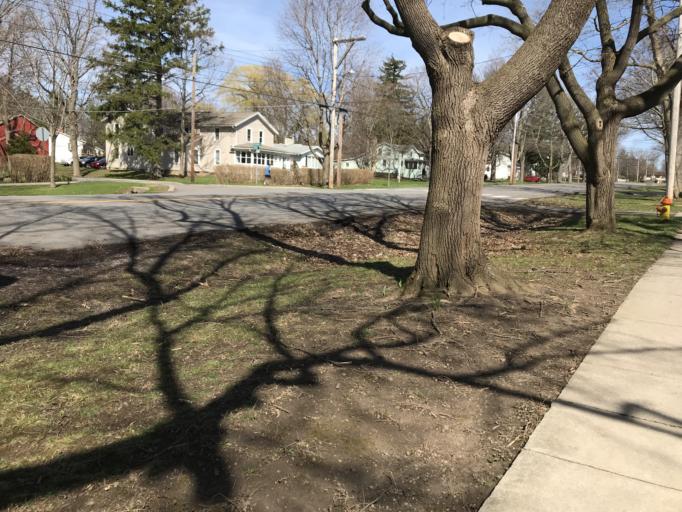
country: US
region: New York
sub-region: Livingston County
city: Geneseo
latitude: 42.7993
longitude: -77.8100
